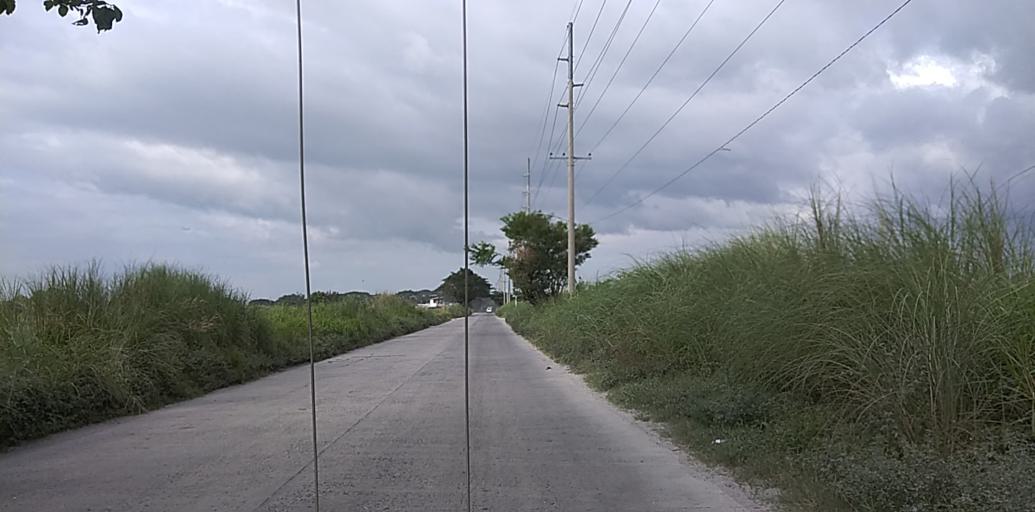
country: PH
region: Central Luzon
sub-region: Province of Pampanga
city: Porac
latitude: 15.0723
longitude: 120.5499
